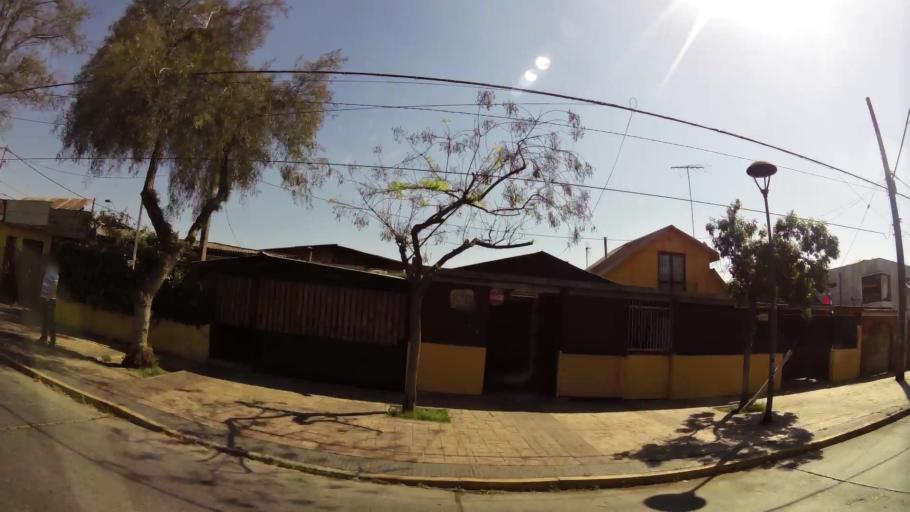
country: CL
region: Santiago Metropolitan
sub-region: Provincia de Santiago
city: La Pintana
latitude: -33.5524
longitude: -70.6248
